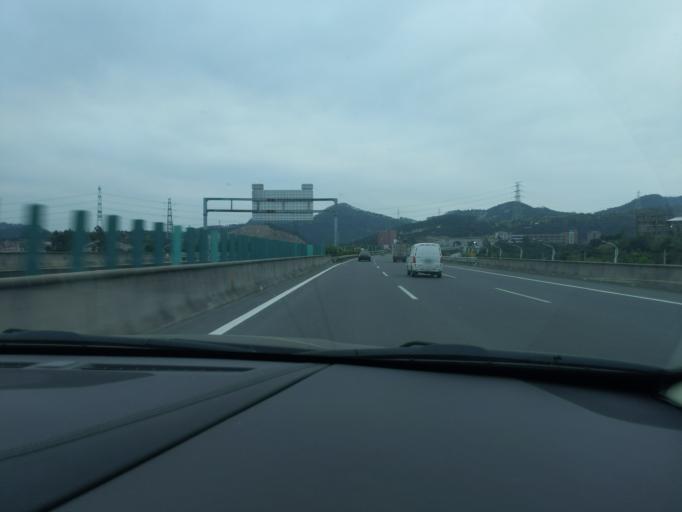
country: CN
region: Fujian
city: Cizao
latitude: 24.7818
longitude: 118.5035
